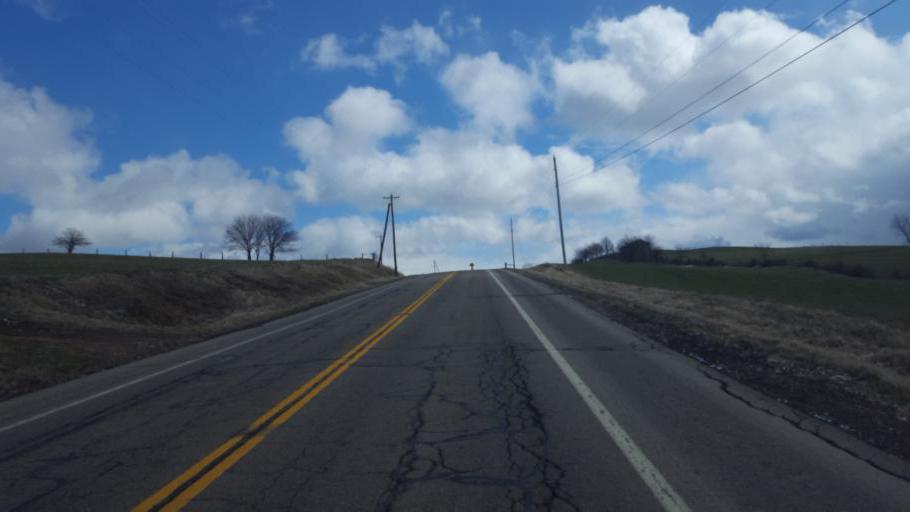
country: US
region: Ohio
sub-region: Tuscarawas County
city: Sugarcreek
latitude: 40.4374
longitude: -81.7496
